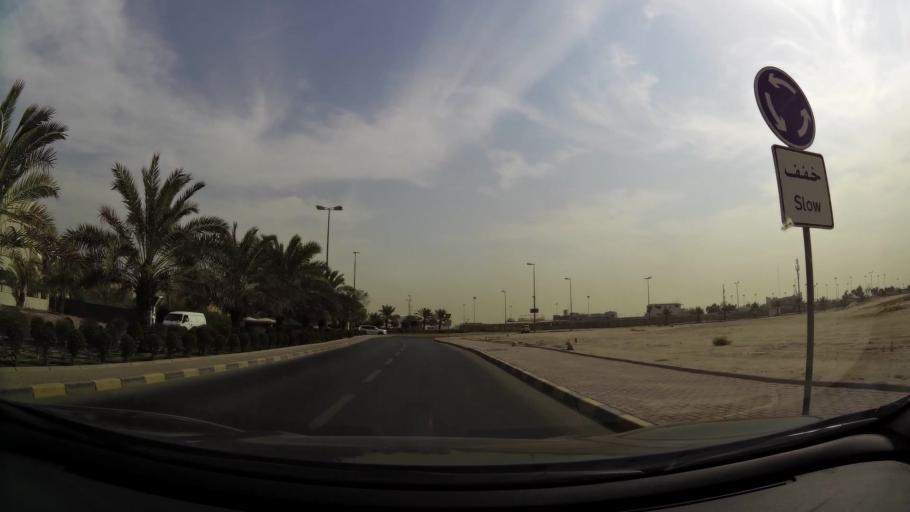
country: KW
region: Al Farwaniyah
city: Janub as Surrah
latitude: 29.2717
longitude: 48.0005
